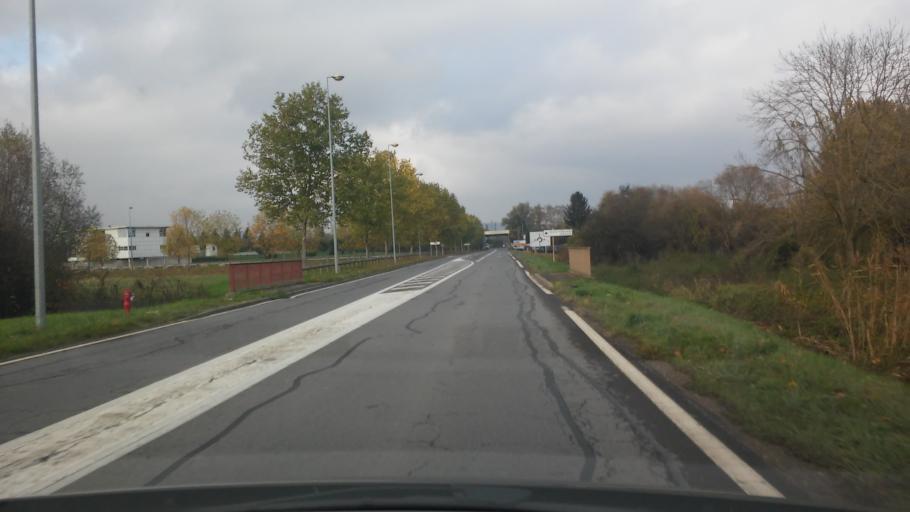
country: FR
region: Lorraine
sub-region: Departement de la Moselle
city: Uckange
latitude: 49.3235
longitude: 6.1541
